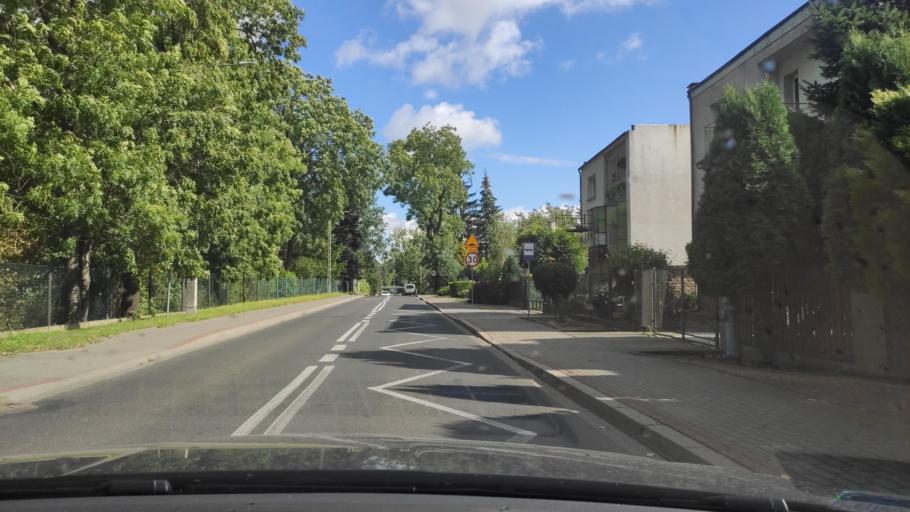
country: PL
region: Greater Poland Voivodeship
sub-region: Powiat poznanski
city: Swarzedz
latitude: 52.4095
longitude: 17.0614
